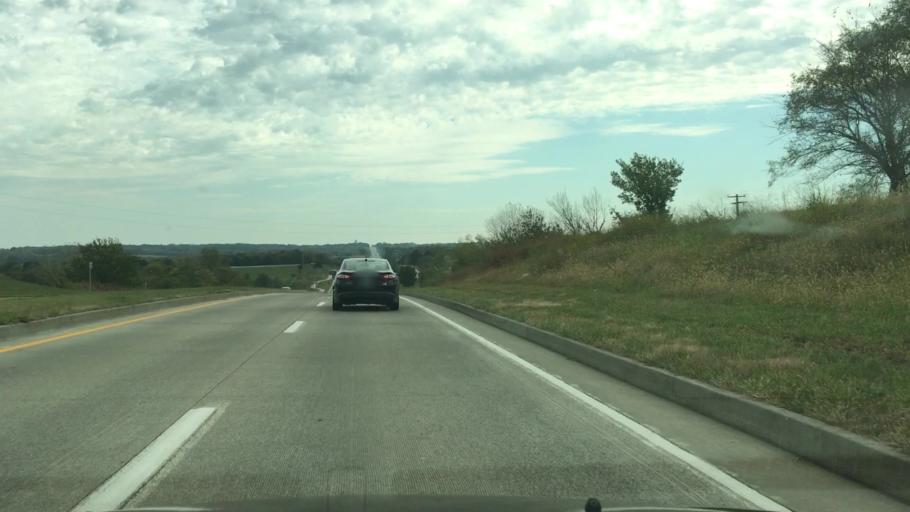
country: US
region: Missouri
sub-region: Jackson County
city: Grandview
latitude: 38.8566
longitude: -94.4876
